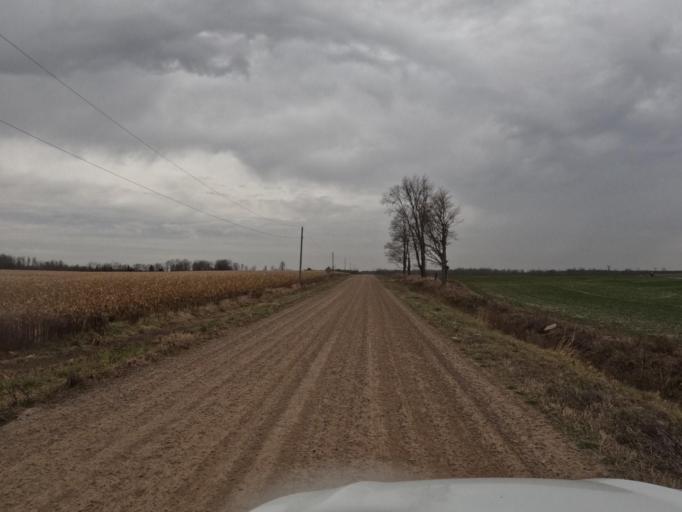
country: CA
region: Ontario
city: Shelburne
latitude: 43.8860
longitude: -80.3822
